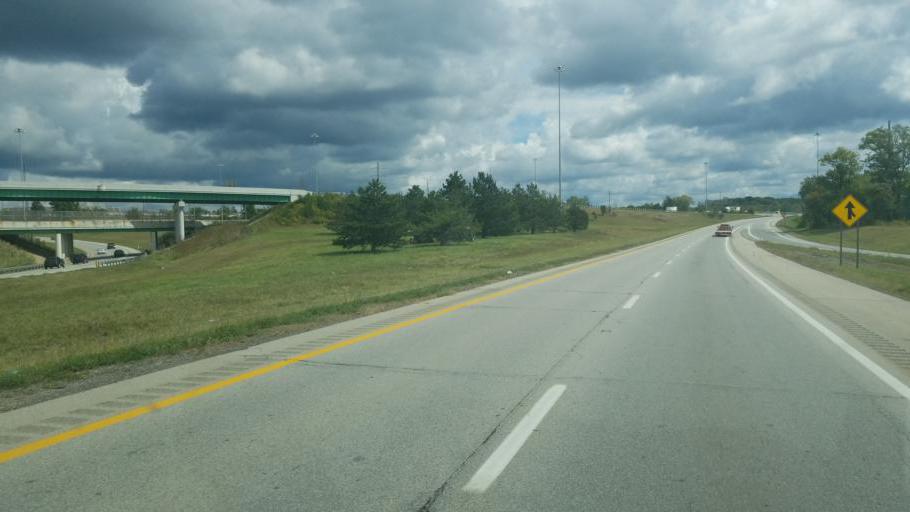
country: US
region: Ohio
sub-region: Cuyahoga County
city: North Randall
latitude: 41.4293
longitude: -81.5036
